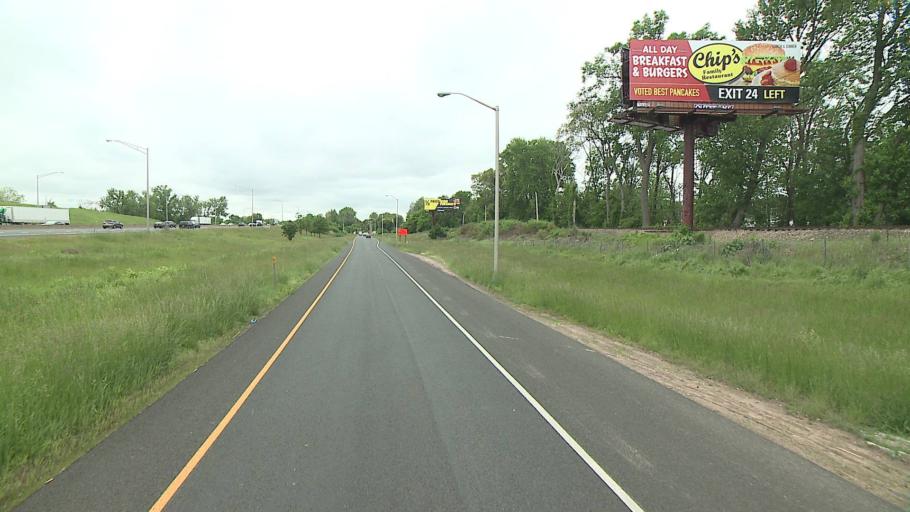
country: US
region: Connecticut
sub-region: Hartford County
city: Wethersfield
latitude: 41.7420
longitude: -72.6637
